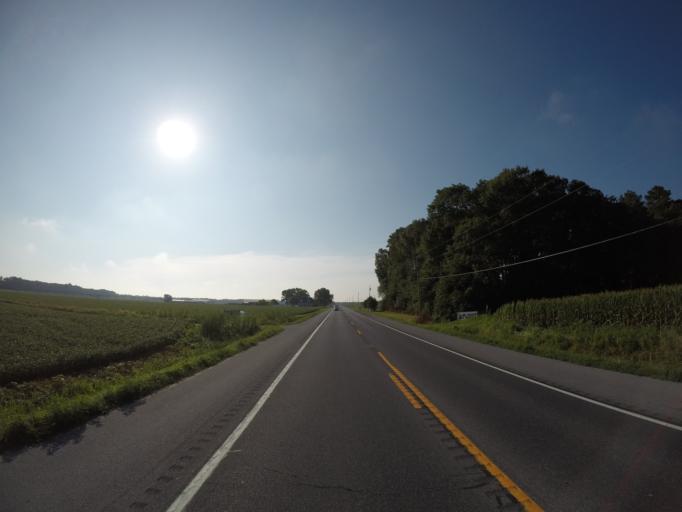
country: US
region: Delaware
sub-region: Sussex County
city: Bridgeville
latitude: 38.7172
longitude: -75.5788
